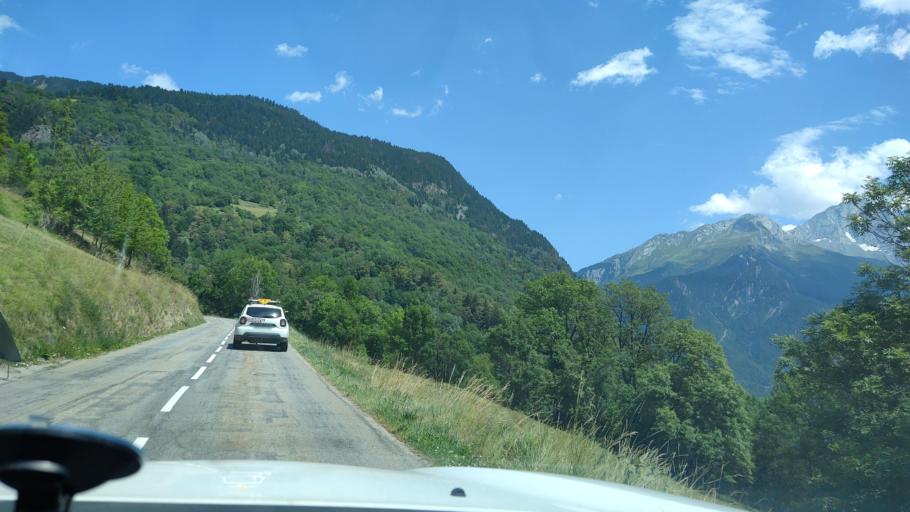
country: FR
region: Rhone-Alpes
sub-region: Departement de la Savoie
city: Bozel
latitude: 45.4466
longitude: 6.6443
